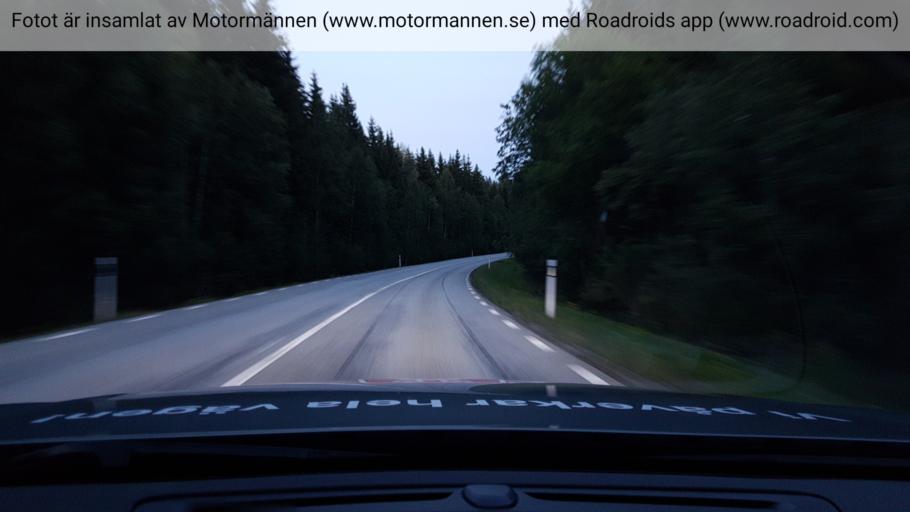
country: SE
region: OErebro
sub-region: Ljusnarsbergs Kommun
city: Kopparberg
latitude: 59.8703
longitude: 15.0326
